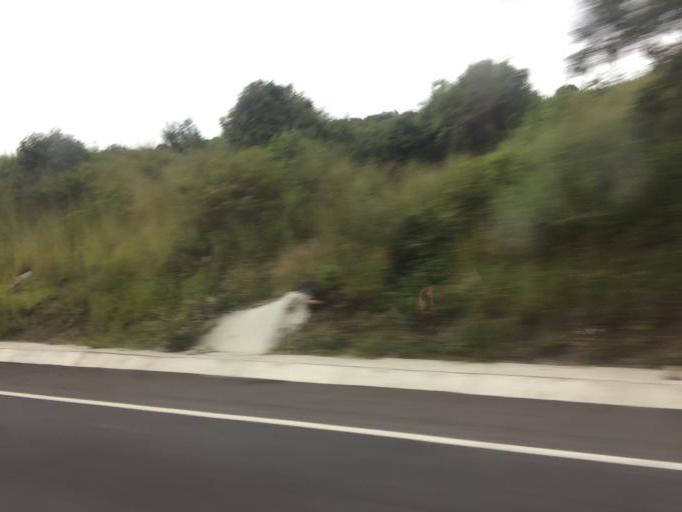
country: MX
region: Jalisco
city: Ocotlan
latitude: 20.4187
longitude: -102.7572
